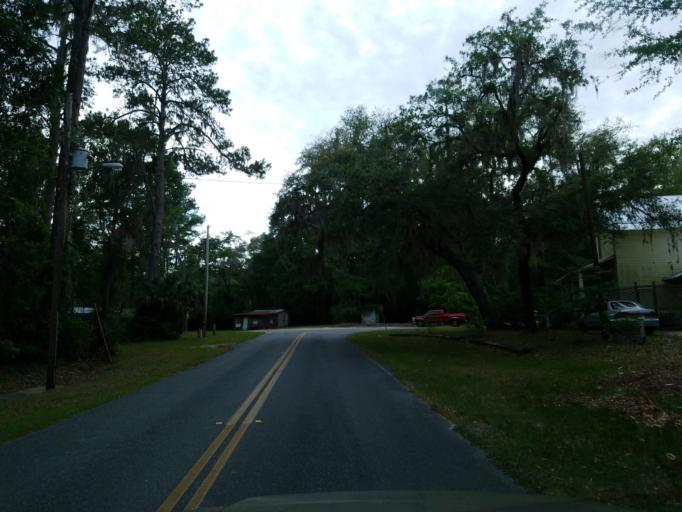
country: US
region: Florida
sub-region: Suwannee County
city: Wellborn
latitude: 30.3321
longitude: -82.7604
